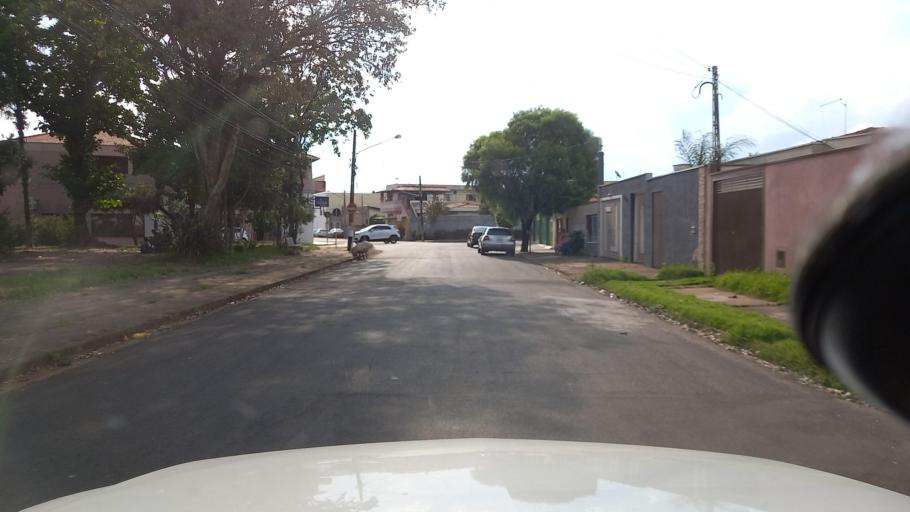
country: BR
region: Sao Paulo
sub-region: Moji-Guacu
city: Mogi-Gaucu
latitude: -22.3488
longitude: -46.9451
